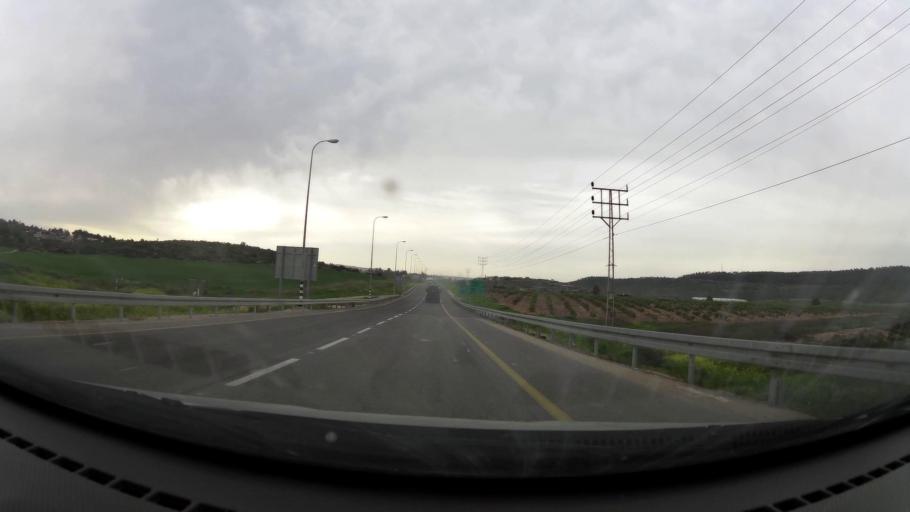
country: IL
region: Jerusalem
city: Bet Shemesh
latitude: 31.6800
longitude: 35.0039
